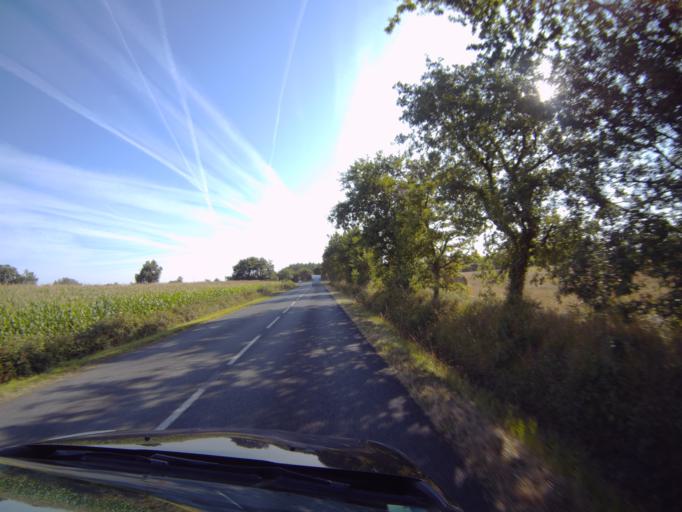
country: FR
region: Pays de la Loire
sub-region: Departement de la Vendee
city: Saint-Hilaire-de-Talmont
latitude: 46.4832
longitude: -1.5884
